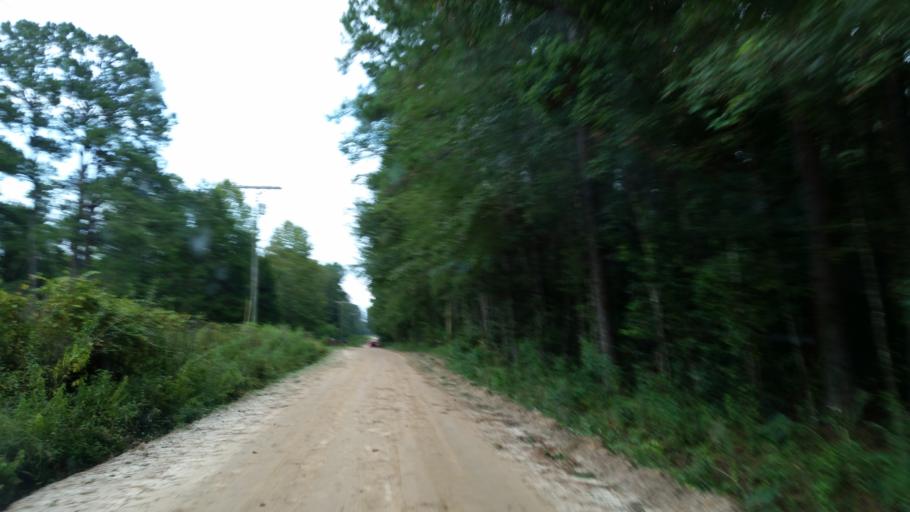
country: US
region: Georgia
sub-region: Lowndes County
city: Valdosta
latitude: 30.7215
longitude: -83.3066
